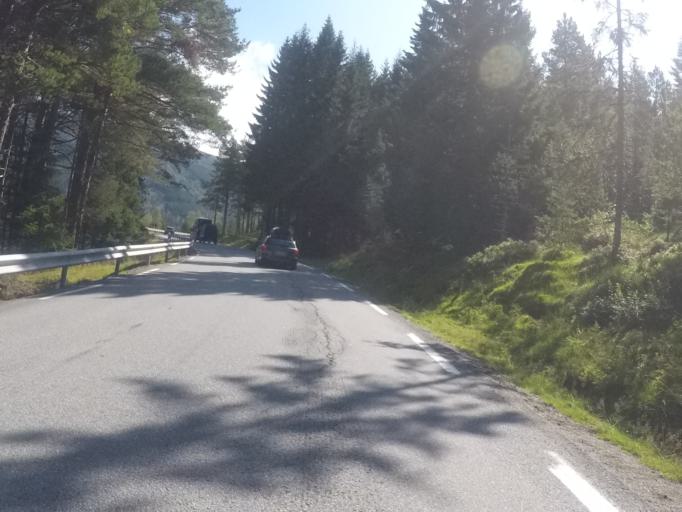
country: NO
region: Sogn og Fjordane
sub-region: Hornindal
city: Hornindal
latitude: 61.7946
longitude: 6.5305
